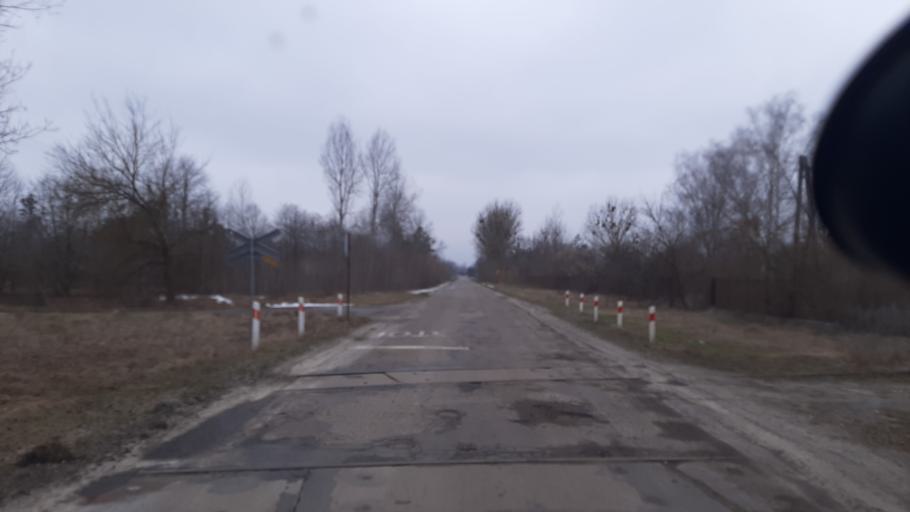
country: PL
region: Lublin Voivodeship
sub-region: Powiat wlodawski
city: Wlodawa
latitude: 51.5195
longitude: 23.5878
